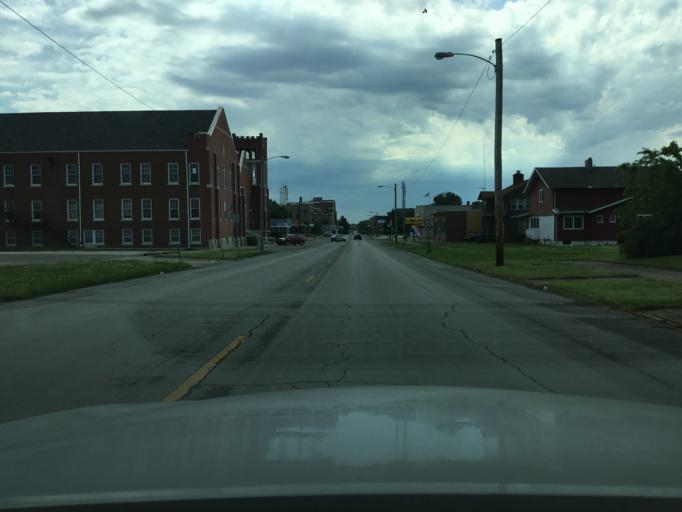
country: US
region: Kansas
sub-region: Montgomery County
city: Coffeyville
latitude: 37.0361
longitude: -95.6221
